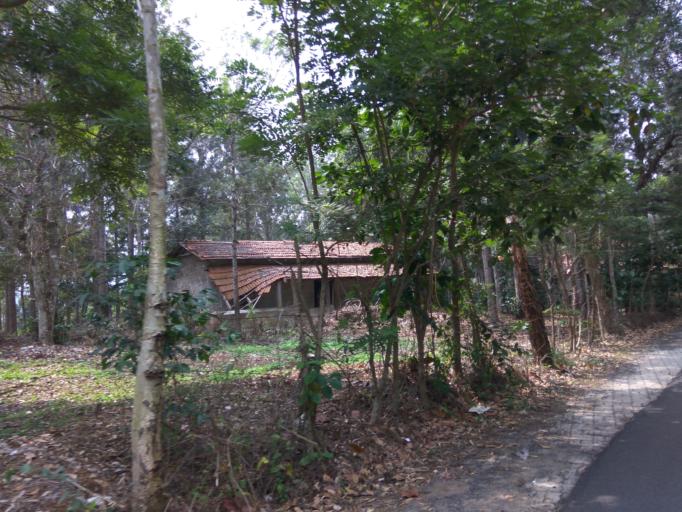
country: IN
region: Tamil Nadu
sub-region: Salem
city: Salem
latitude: 11.7756
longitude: 78.2207
